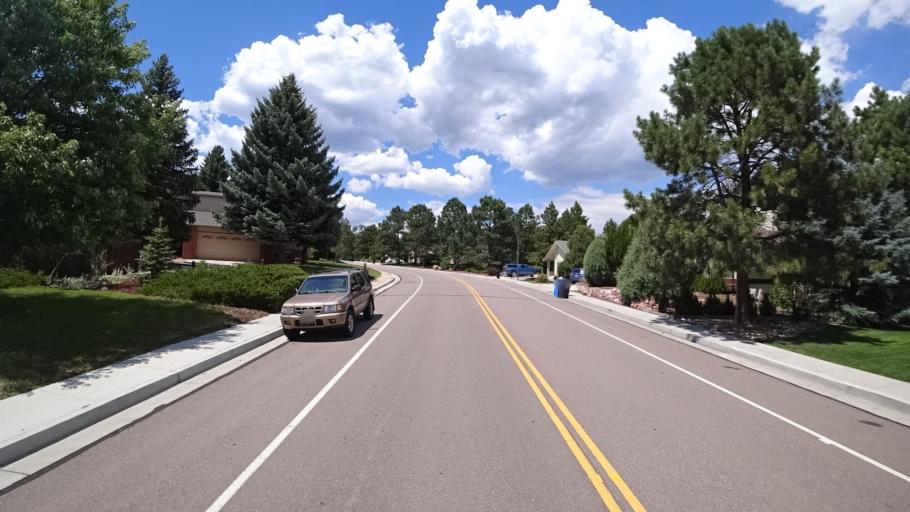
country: US
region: Colorado
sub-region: El Paso County
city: Air Force Academy
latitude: 38.9354
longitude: -104.8364
